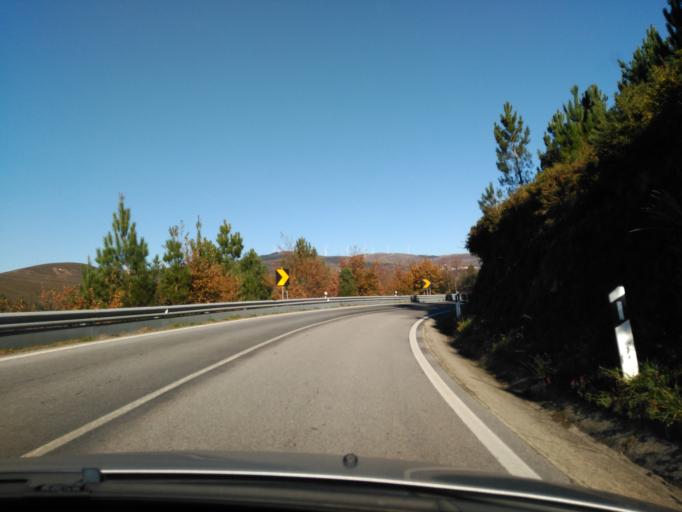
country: PT
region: Braga
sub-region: Cabeceiras de Basto
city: Cabeceiras de Basto
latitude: 41.6842
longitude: -7.9570
